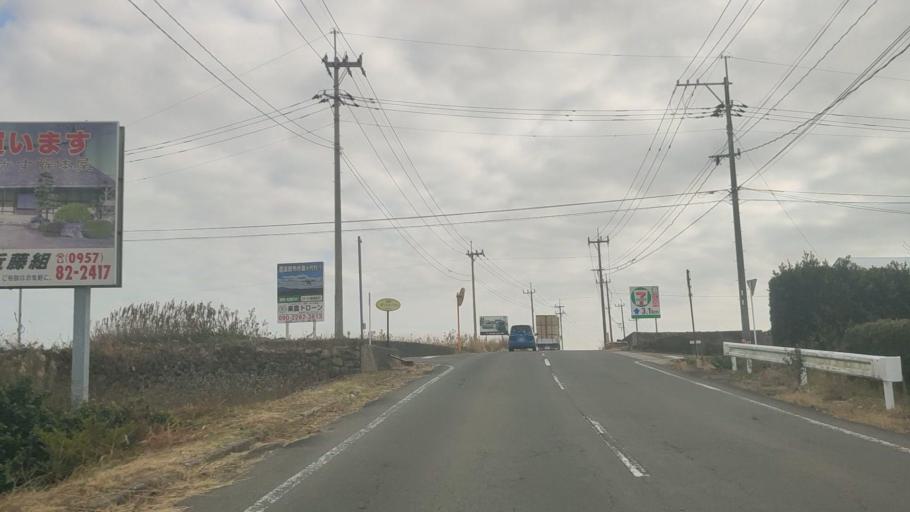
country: JP
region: Nagasaki
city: Shimabara
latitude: 32.8536
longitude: 130.2515
